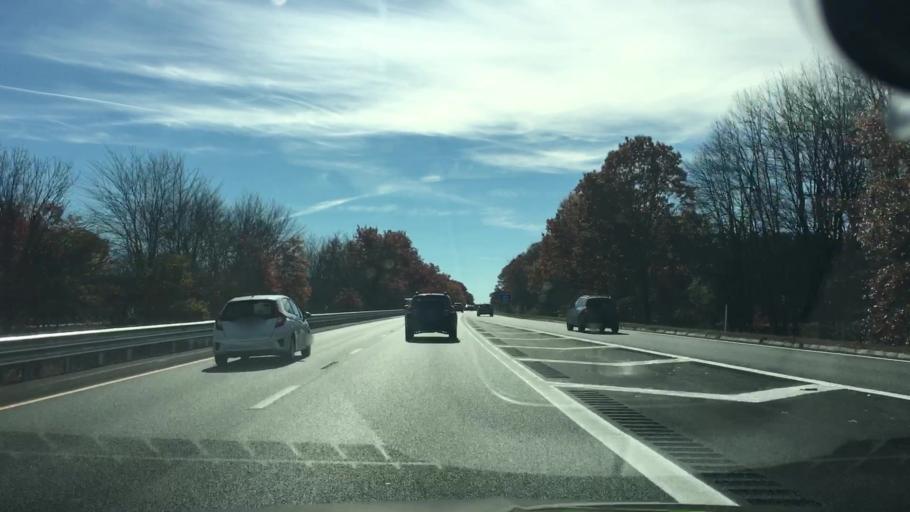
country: US
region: Massachusetts
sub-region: Franklin County
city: South Deerfield
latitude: 42.4637
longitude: -72.6166
